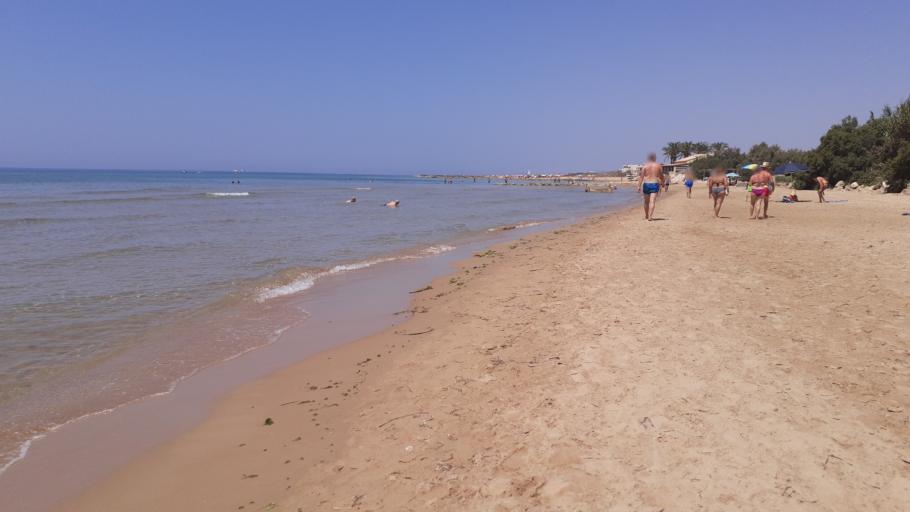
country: IT
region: Sicily
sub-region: Ragusa
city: Donnalucata
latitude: 36.7475
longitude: 14.6601
